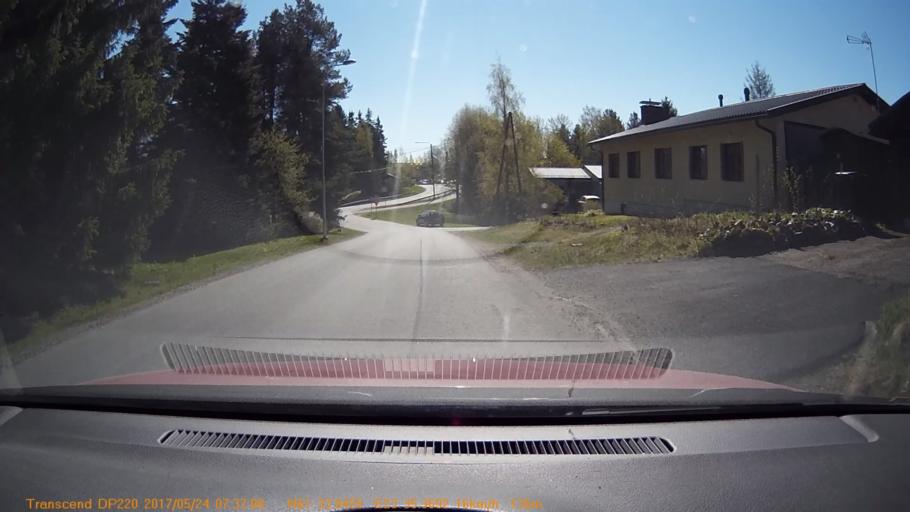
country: FI
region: Pirkanmaa
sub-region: Tampere
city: Yloejaervi
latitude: 61.5657
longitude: 23.5895
